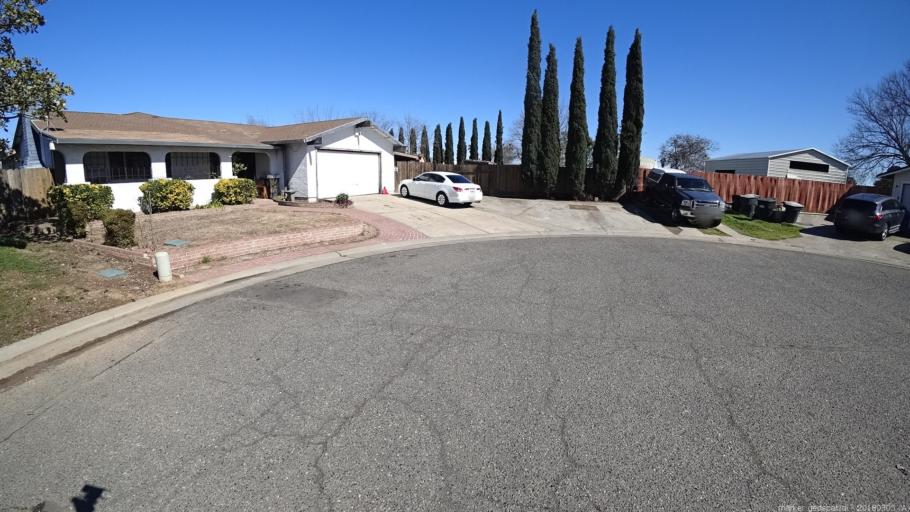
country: US
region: California
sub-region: Sacramento County
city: Florin
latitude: 38.4904
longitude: -121.3818
